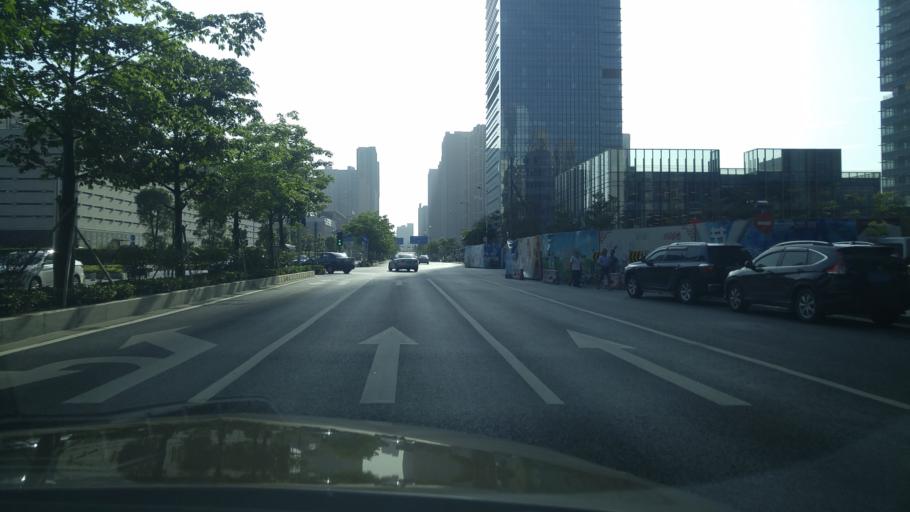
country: CN
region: Guangdong
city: Foshan
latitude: 23.0652
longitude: 113.1471
